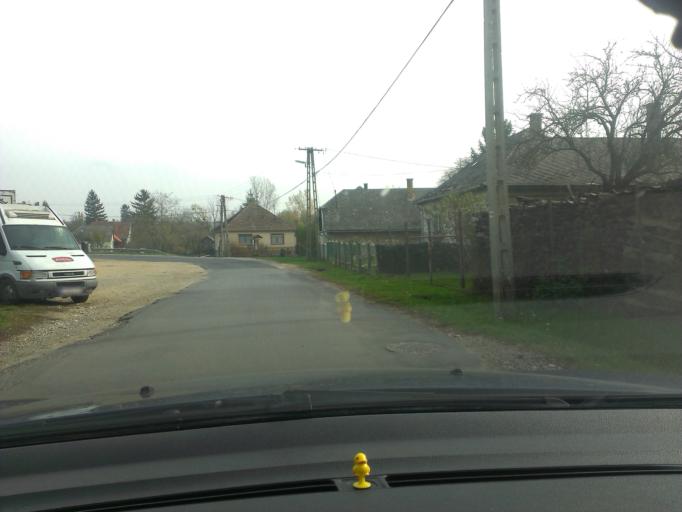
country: HU
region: Gyor-Moson-Sopron
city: Bakonyszentlaszlo
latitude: 47.3562
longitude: 17.8834
